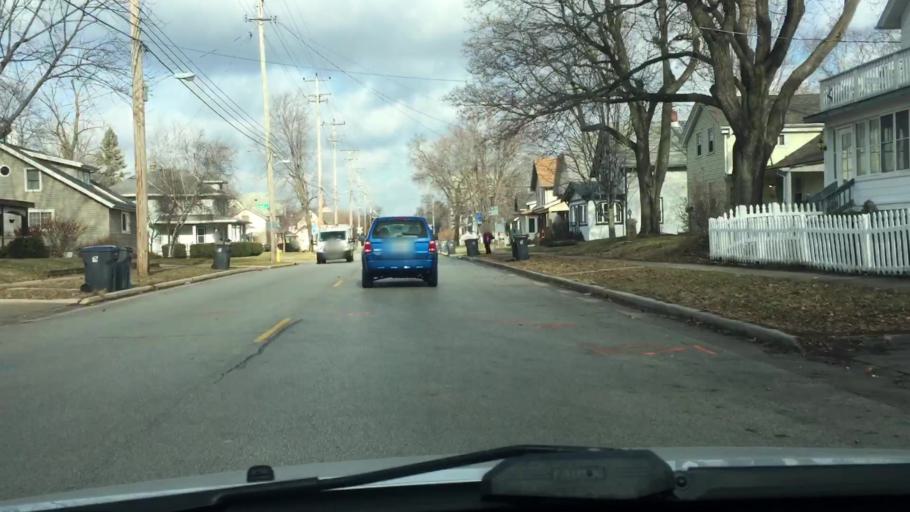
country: US
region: Wisconsin
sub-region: Waukesha County
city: Waukesha
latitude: 43.0037
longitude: -88.2367
